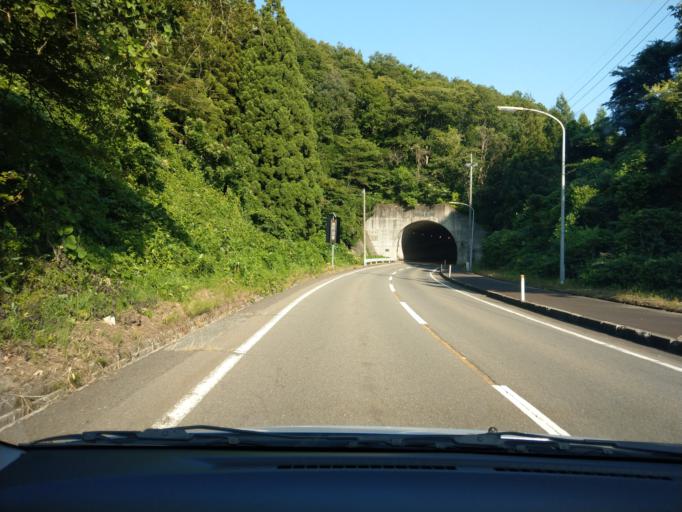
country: JP
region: Akita
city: Akita
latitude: 39.6066
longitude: 140.2059
